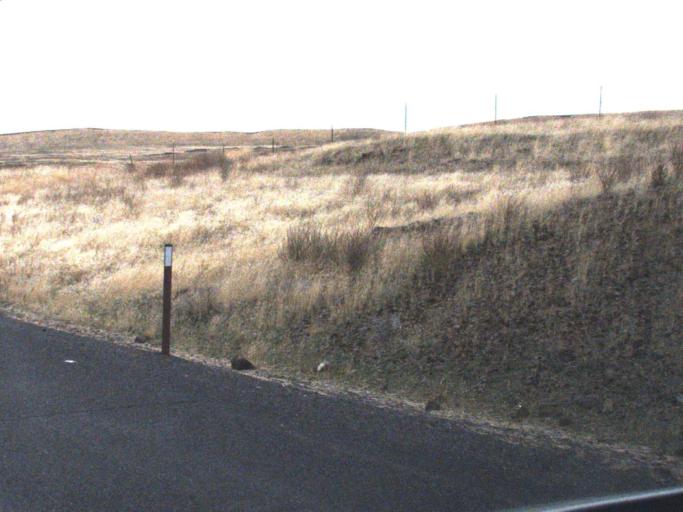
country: US
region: Washington
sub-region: Adams County
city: Ritzville
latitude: 46.7645
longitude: -118.1634
